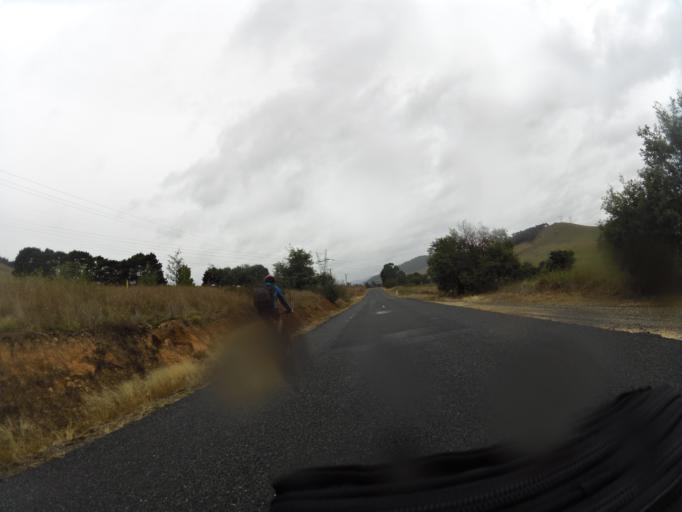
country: AU
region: New South Wales
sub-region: Greater Hume Shire
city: Holbrook
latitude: -36.2246
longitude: 147.6606
